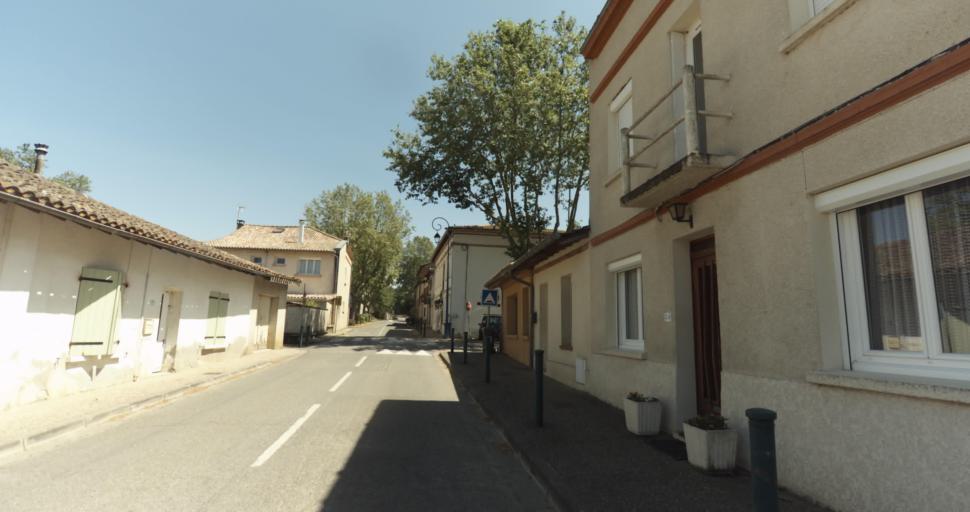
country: FR
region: Midi-Pyrenees
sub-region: Departement de la Haute-Garonne
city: Levignac
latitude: 43.6390
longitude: 1.1683
